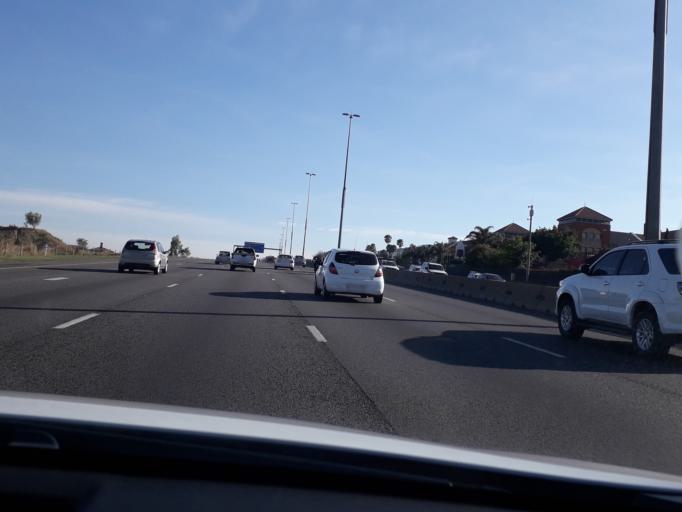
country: ZA
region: Gauteng
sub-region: City of Johannesburg Metropolitan Municipality
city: Midrand
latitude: -25.9459
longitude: 28.1369
